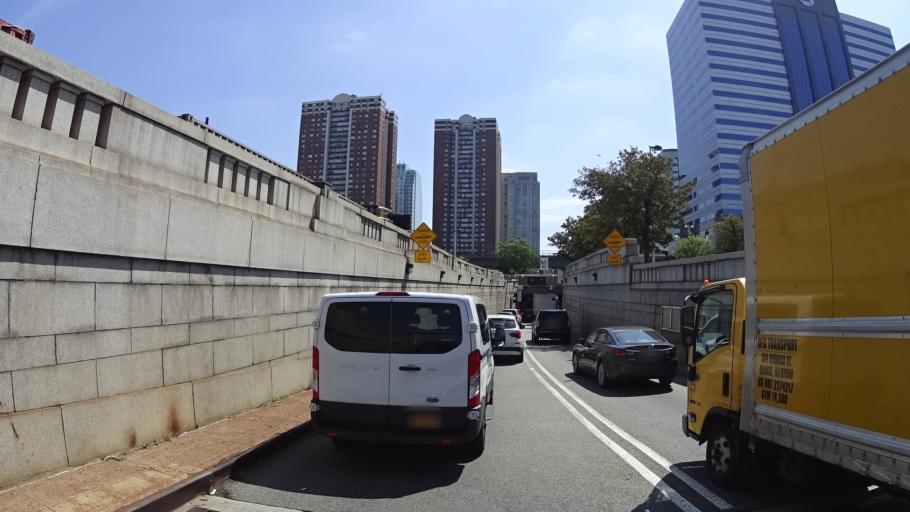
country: US
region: New Jersey
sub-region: Hudson County
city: Hoboken
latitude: 40.7298
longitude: -74.0372
